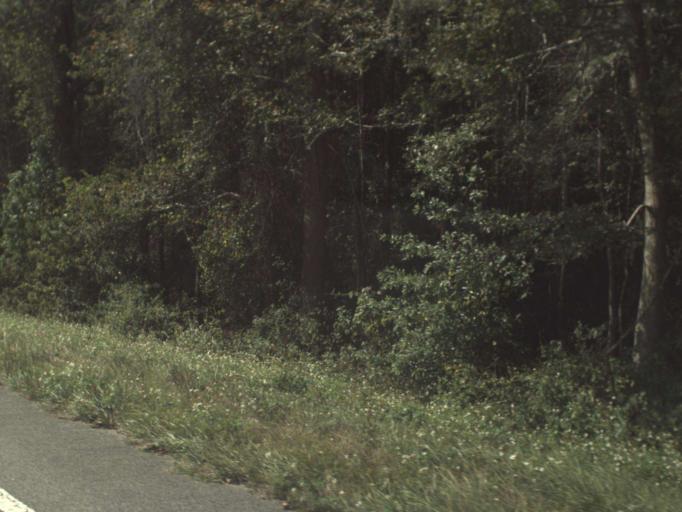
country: US
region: Florida
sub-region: Washington County
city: Chipley
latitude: 30.5608
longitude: -85.6183
